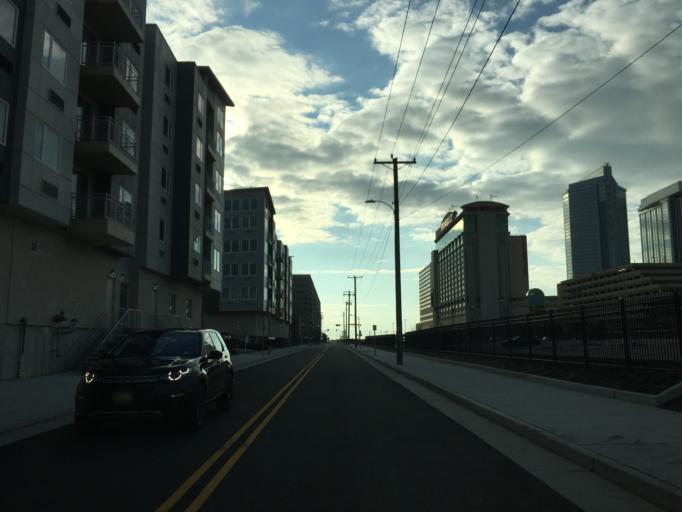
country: US
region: New Jersey
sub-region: Atlantic County
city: Atlantic City
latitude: 39.3654
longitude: -74.4191
